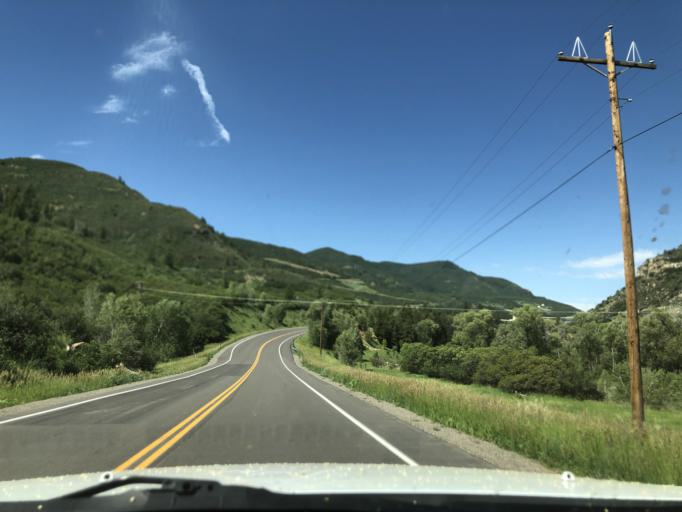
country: US
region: Colorado
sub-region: Delta County
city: Paonia
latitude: 38.9293
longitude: -107.4203
